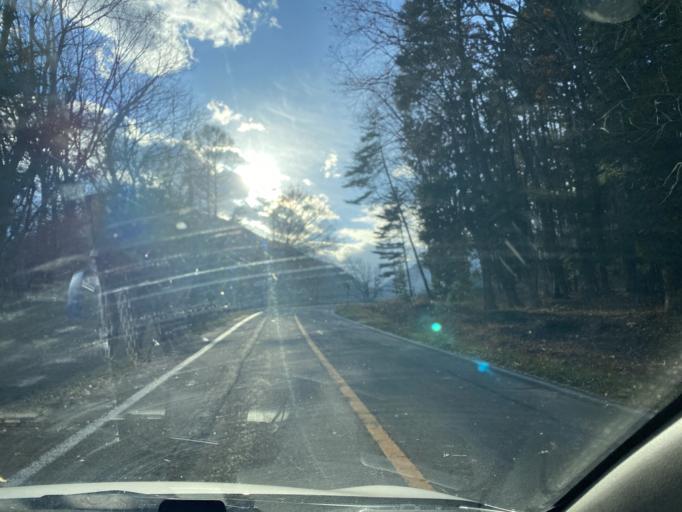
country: JP
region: Nagano
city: Omachi
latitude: 36.5221
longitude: 137.8050
